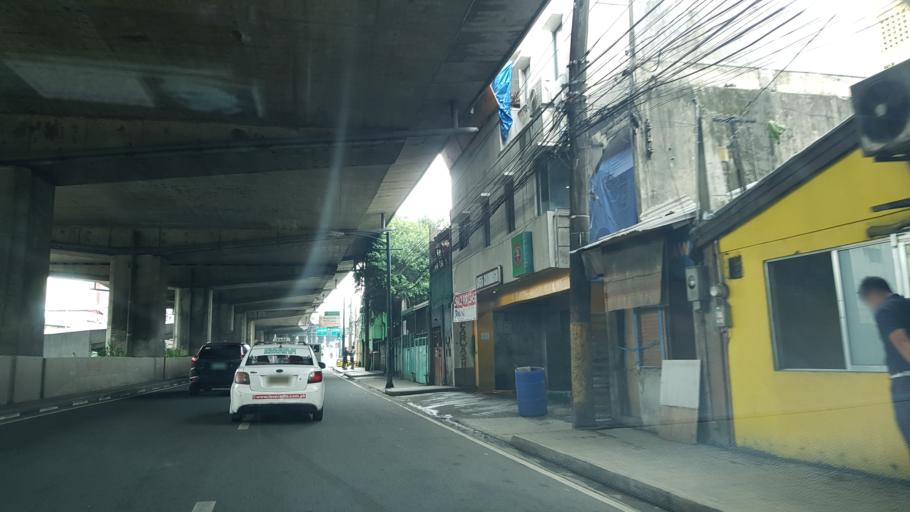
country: PH
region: Metro Manila
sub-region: Makati City
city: Makati City
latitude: 14.5574
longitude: 121.0418
